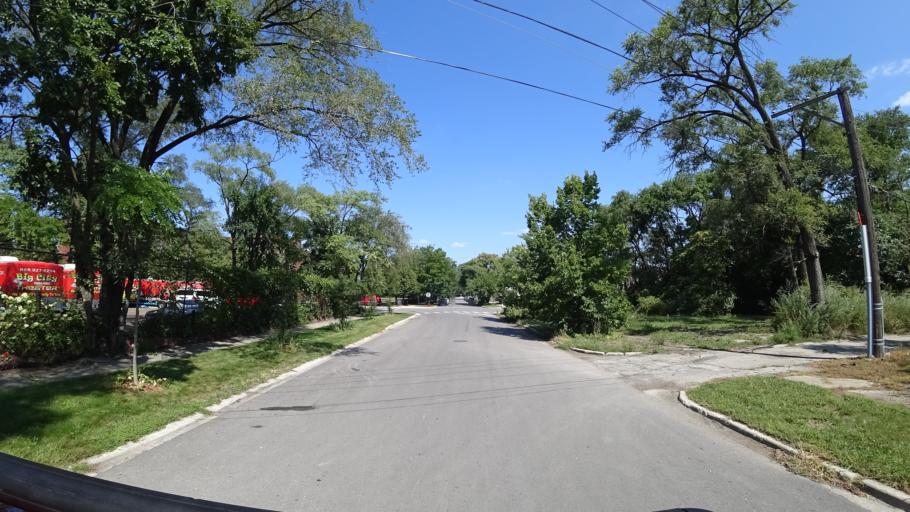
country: US
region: Illinois
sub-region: Cook County
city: Cicero
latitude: 41.8708
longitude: -87.7315
